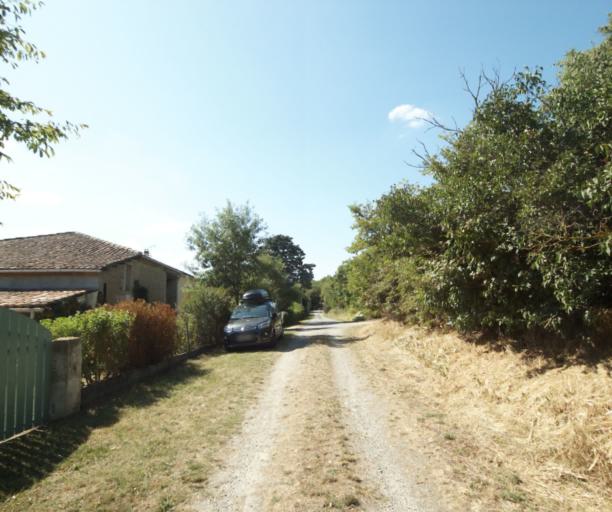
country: FR
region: Midi-Pyrenees
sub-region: Departement de la Haute-Garonne
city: Saint-Felix-Lauragais
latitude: 43.4862
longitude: 1.9030
